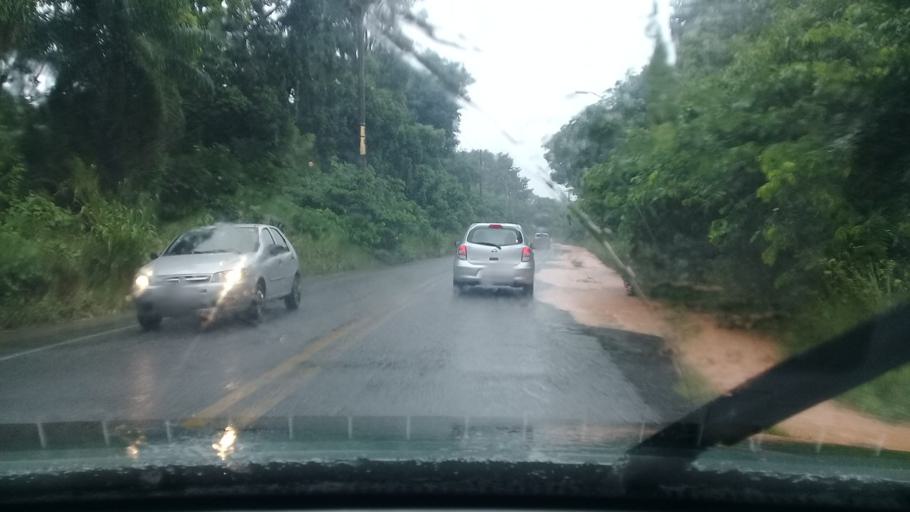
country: BR
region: Pernambuco
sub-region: Paulista
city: Paulista
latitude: -7.9476
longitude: -34.8821
